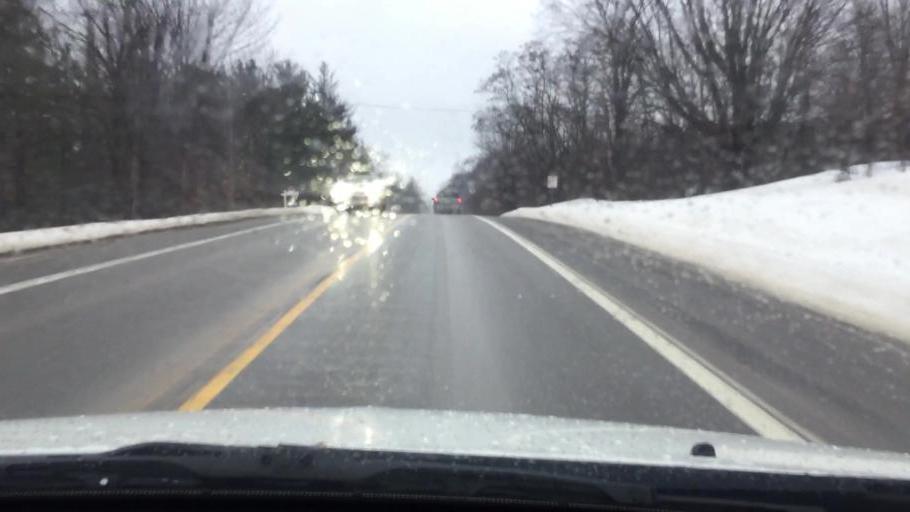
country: US
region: Michigan
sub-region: Charlevoix County
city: East Jordan
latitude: 45.2439
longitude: -85.1809
